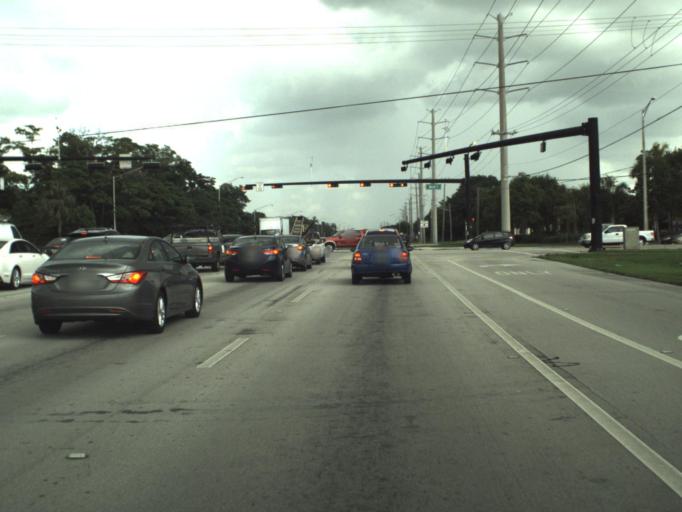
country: US
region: Florida
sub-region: Broward County
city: Coconut Creek
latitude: 26.2855
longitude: -80.2018
